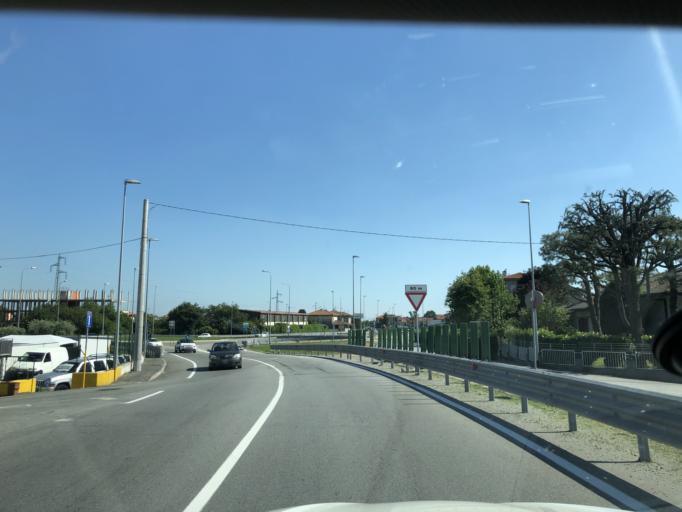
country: IT
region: Piedmont
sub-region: Provincia di Novara
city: Oleggio
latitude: 45.6008
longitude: 8.6442
